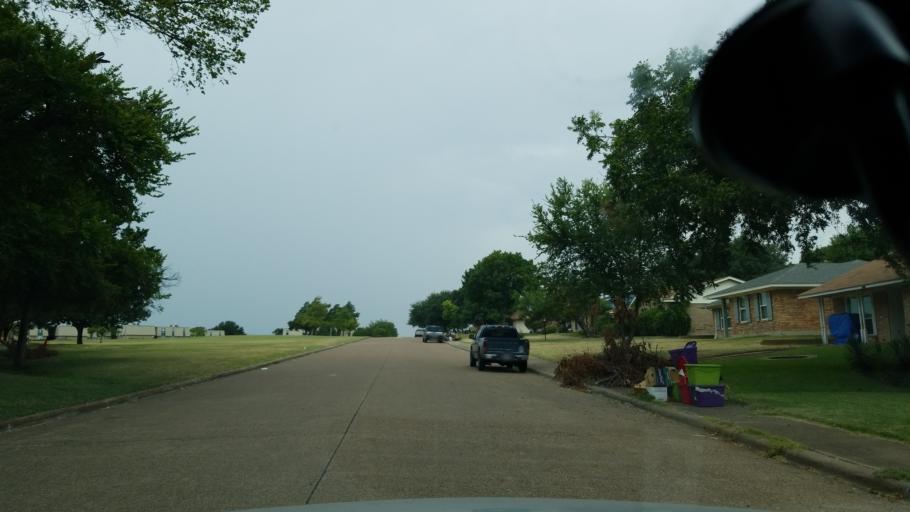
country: US
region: Texas
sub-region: Dallas County
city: Cockrell Hill
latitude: 32.6848
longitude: -96.8526
